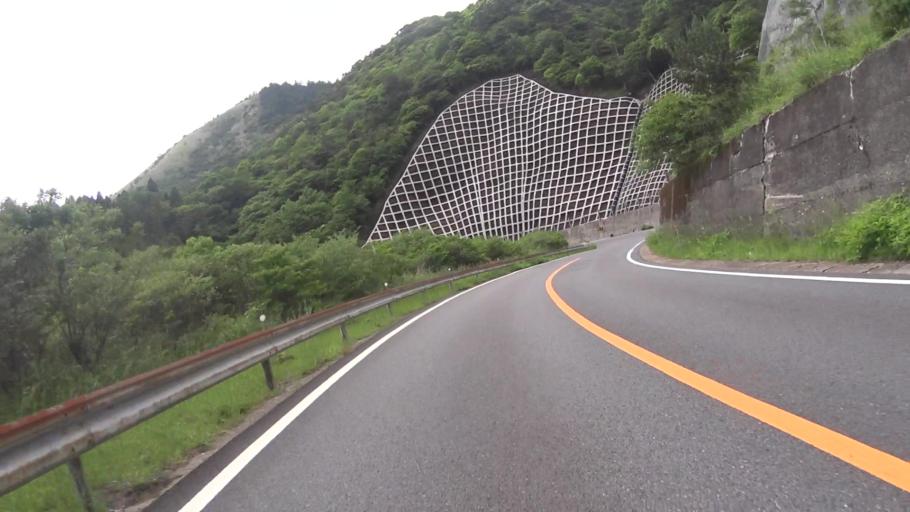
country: JP
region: Kumamoto
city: Aso
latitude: 33.0862
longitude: 131.1913
